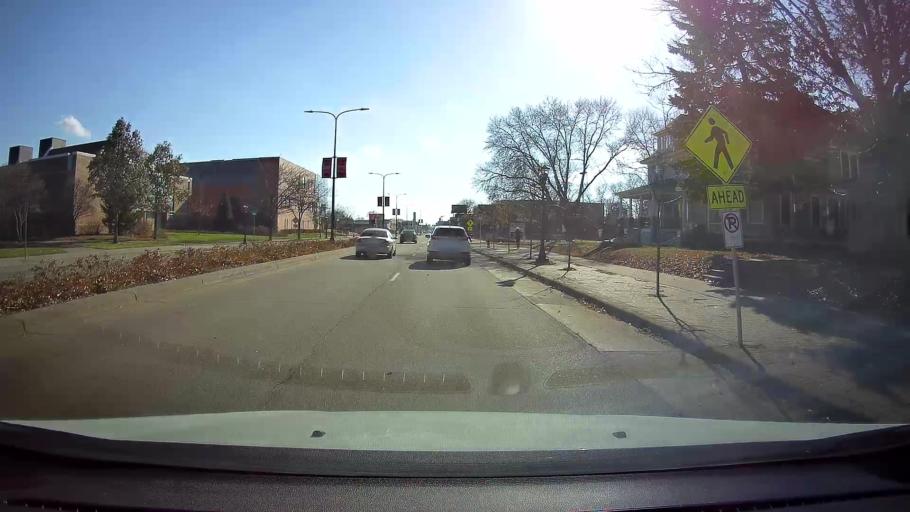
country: US
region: Minnesota
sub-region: Ramsey County
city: Falcon Heights
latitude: 44.9658
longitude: -93.1672
